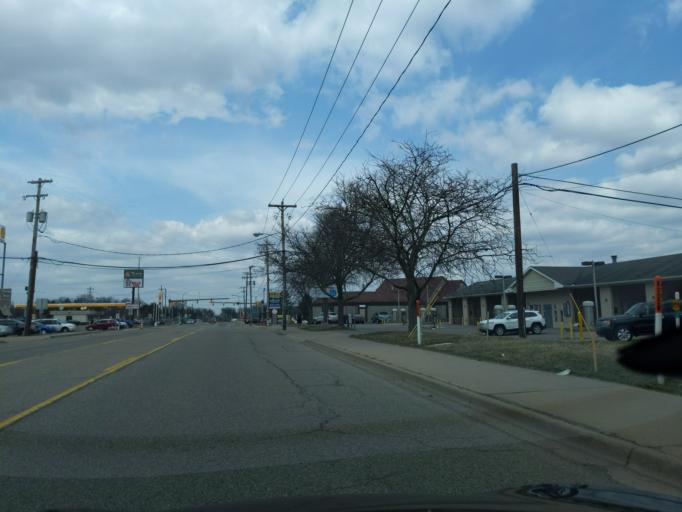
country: US
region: Michigan
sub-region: Calhoun County
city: Lakeview
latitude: 42.2595
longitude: -85.1985
